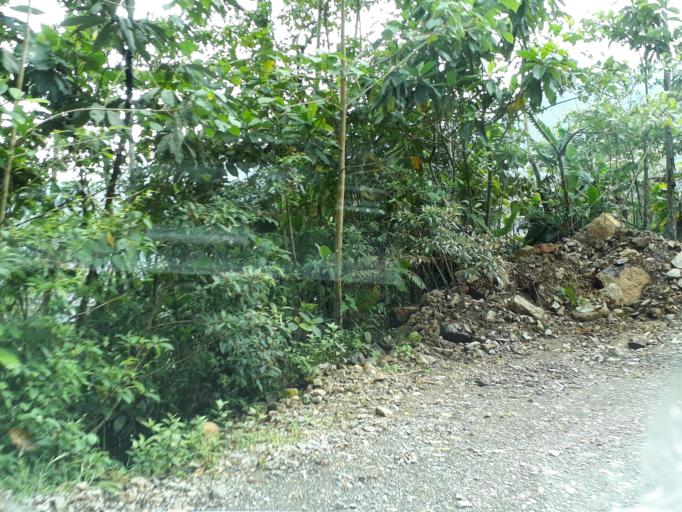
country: CO
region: Cundinamarca
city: Gachala
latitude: 4.7130
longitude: -73.3739
